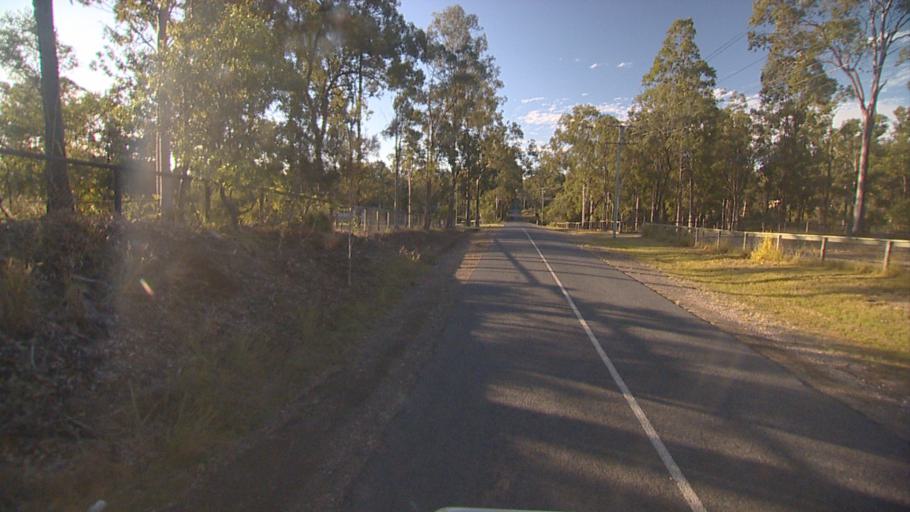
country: AU
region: Queensland
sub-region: Logan
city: Waterford West
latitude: -27.7321
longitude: 153.1460
